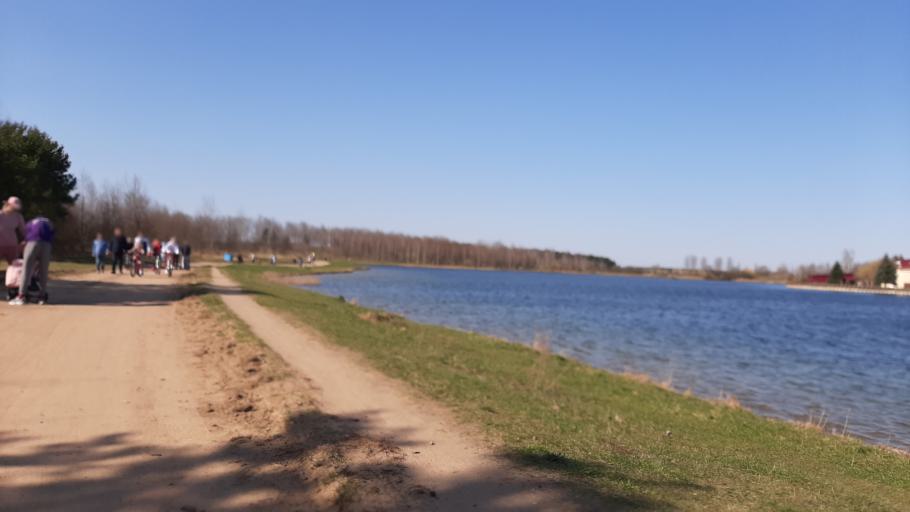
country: BY
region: Minsk
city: Bal'shavik
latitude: 53.9579
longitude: 27.5717
